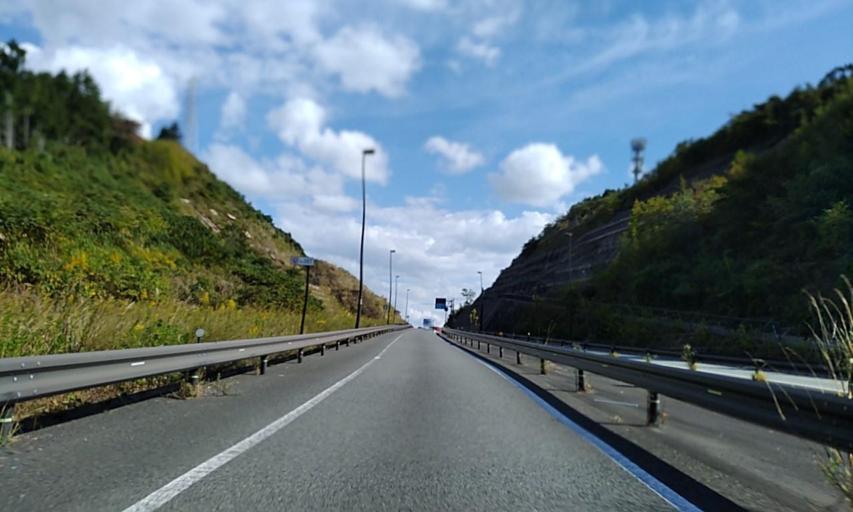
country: JP
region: Wakayama
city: Tanabe
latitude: 33.7507
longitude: 135.3571
